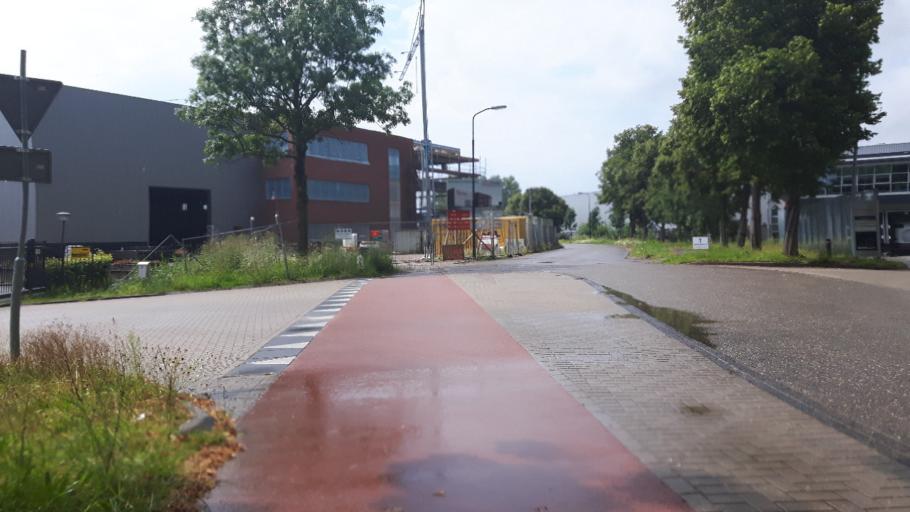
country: NL
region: Utrecht
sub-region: Gemeente Montfoort
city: Montfoort
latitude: 52.0426
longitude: 4.9355
